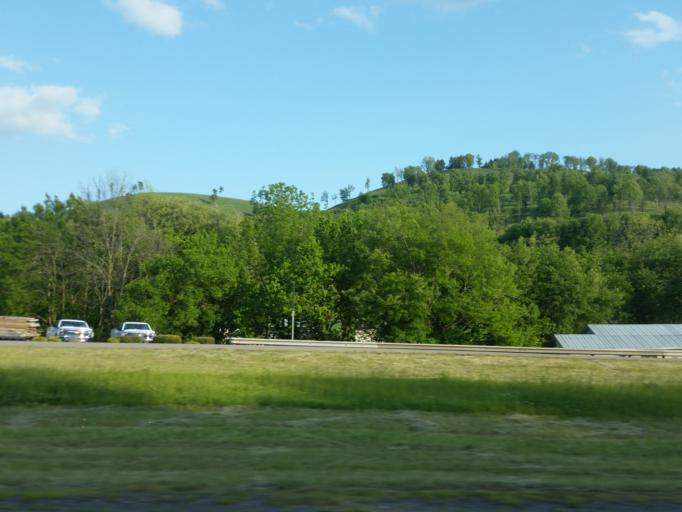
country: US
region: Virginia
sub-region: Russell County
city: Honaker
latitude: 36.9556
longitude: -81.9423
